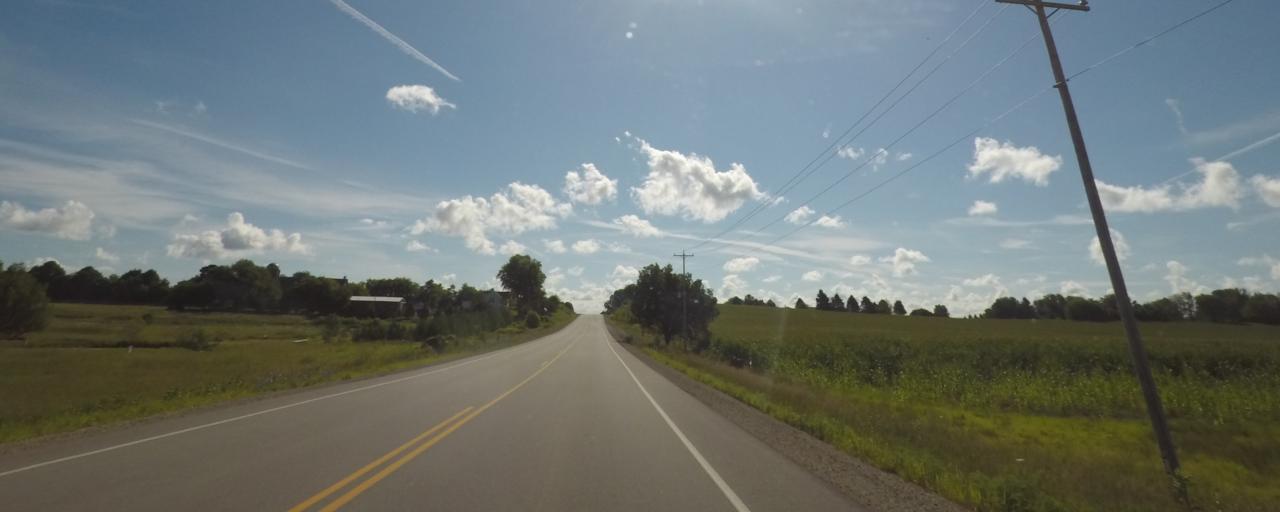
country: US
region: Wisconsin
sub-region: Jefferson County
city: Ixonia
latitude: 43.0678
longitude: -88.6230
